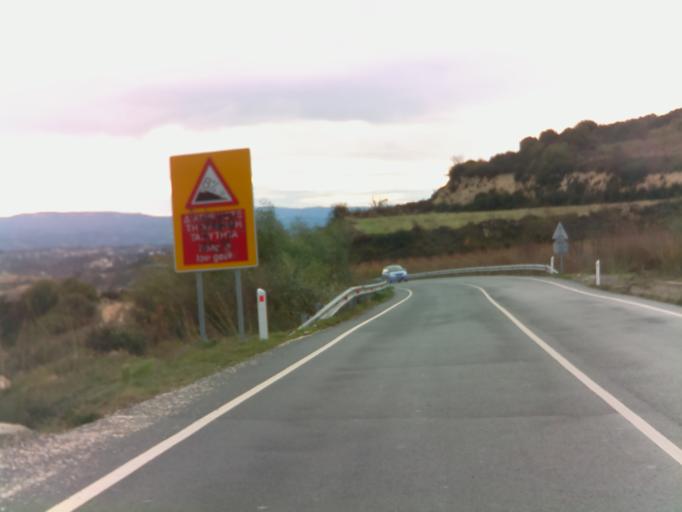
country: CY
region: Pafos
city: Tala
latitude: 34.8997
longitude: 32.4499
